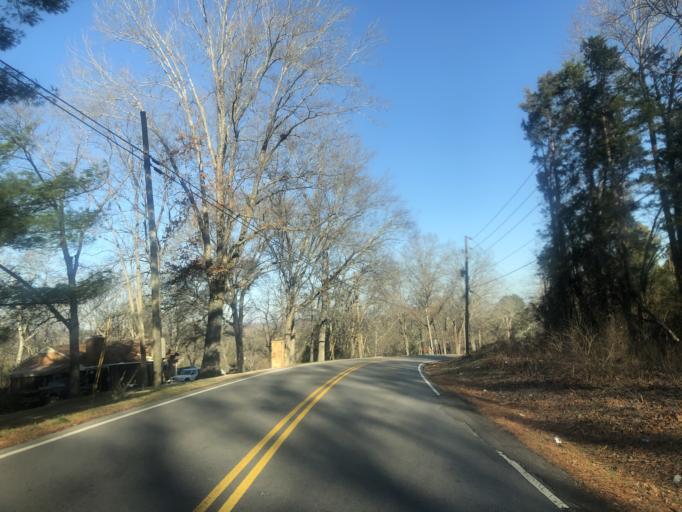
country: US
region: Tennessee
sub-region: Williamson County
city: Nolensville
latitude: 36.0192
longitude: -86.6648
